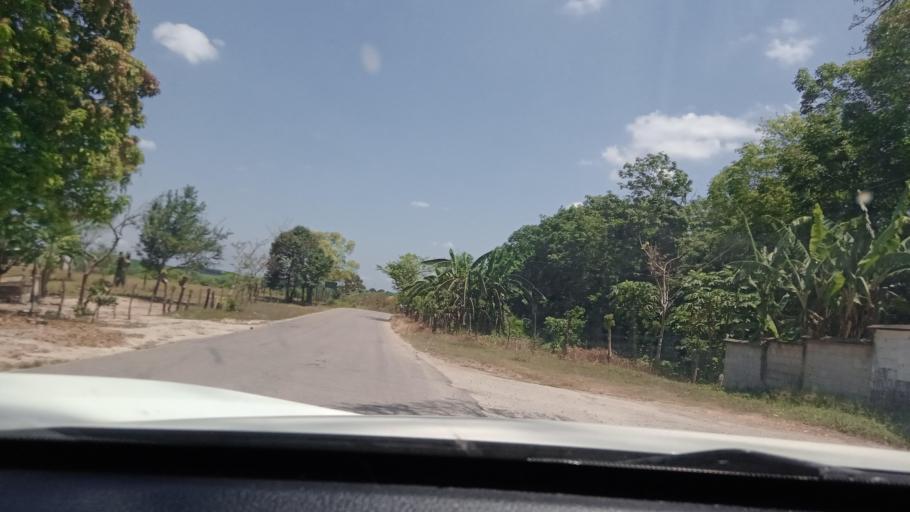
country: MX
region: Veracruz
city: Las Choapas
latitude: 17.7560
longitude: -94.1116
